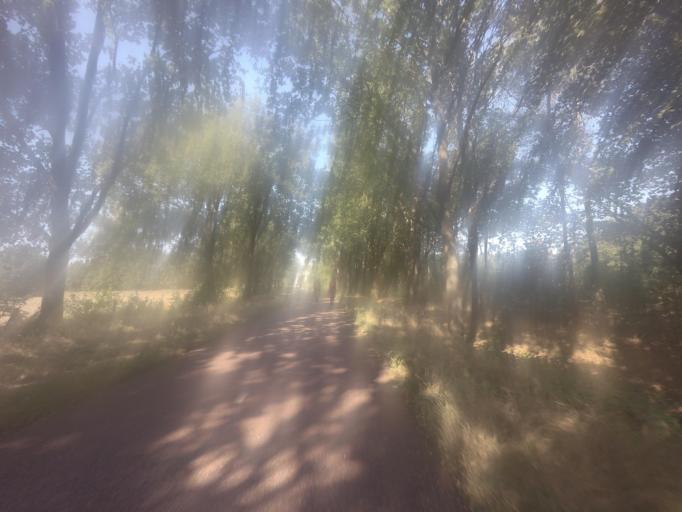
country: NL
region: North Brabant
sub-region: Gemeente Goirle
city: Goirle
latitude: 51.5385
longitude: 5.0330
